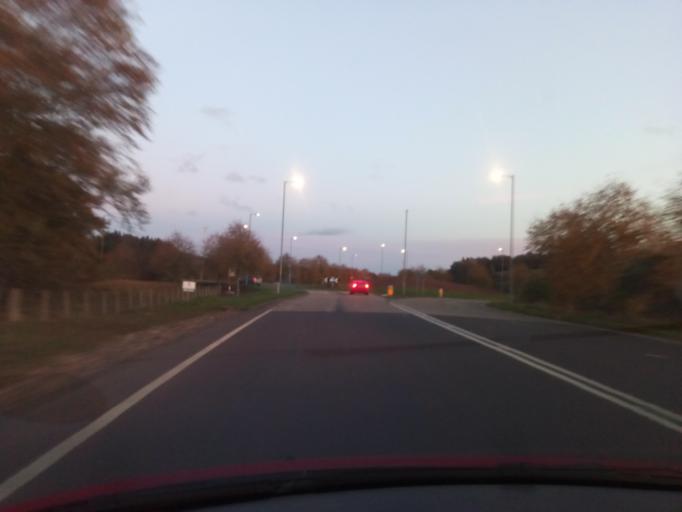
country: GB
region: Scotland
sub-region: The Scottish Borders
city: Lauder
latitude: 55.7716
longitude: -2.7886
